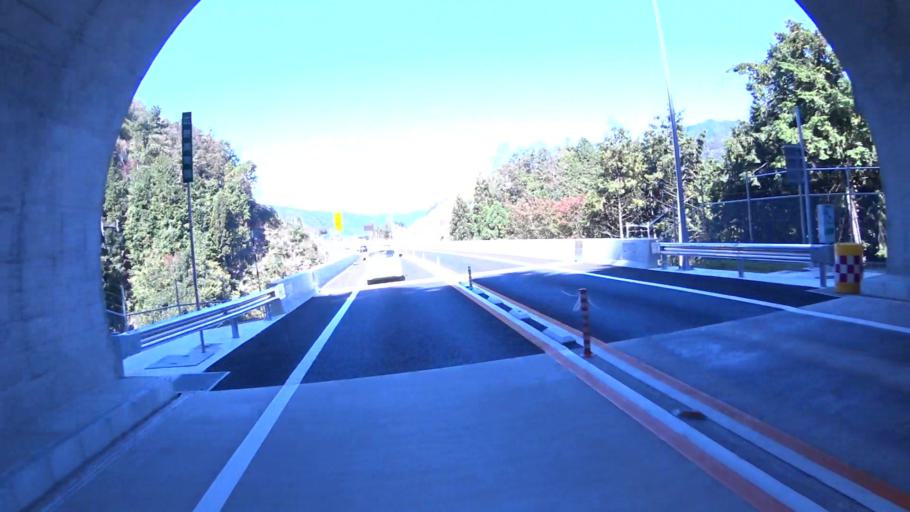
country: JP
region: Kyoto
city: Ayabe
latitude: 35.2697
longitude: 135.3443
